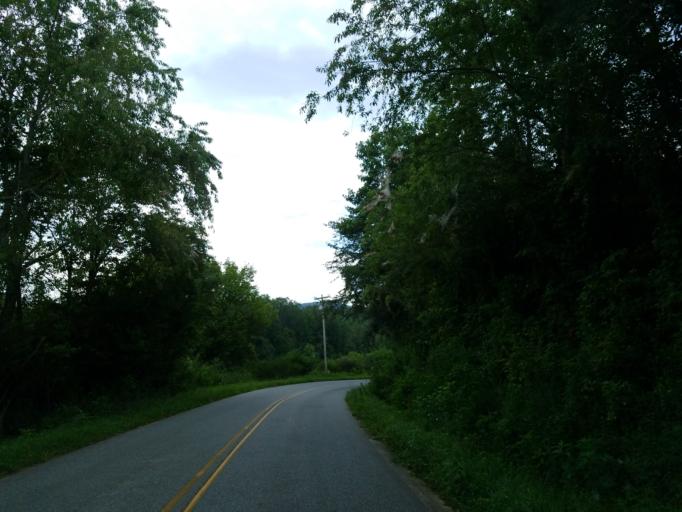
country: US
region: Georgia
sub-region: Fannin County
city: Blue Ridge
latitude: 34.8447
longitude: -84.2280
